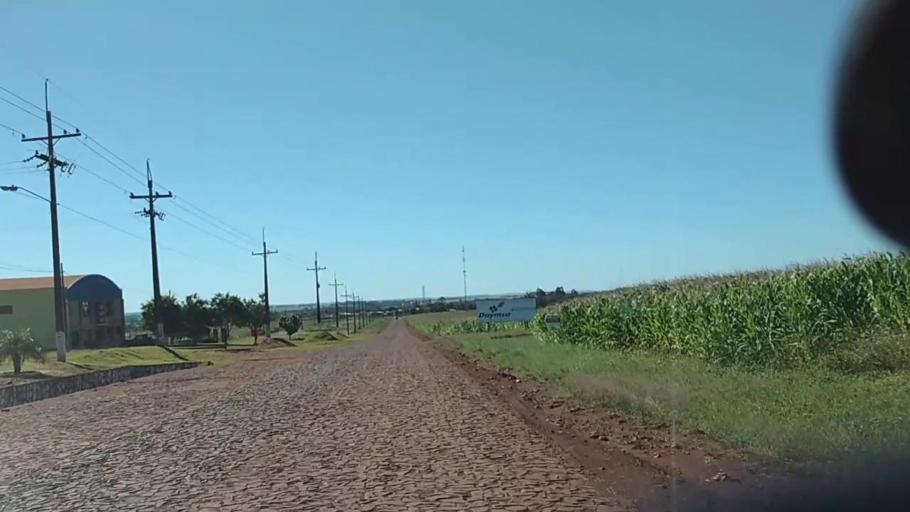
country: PY
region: Alto Parana
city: Naranjal
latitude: -25.9741
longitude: -55.2110
